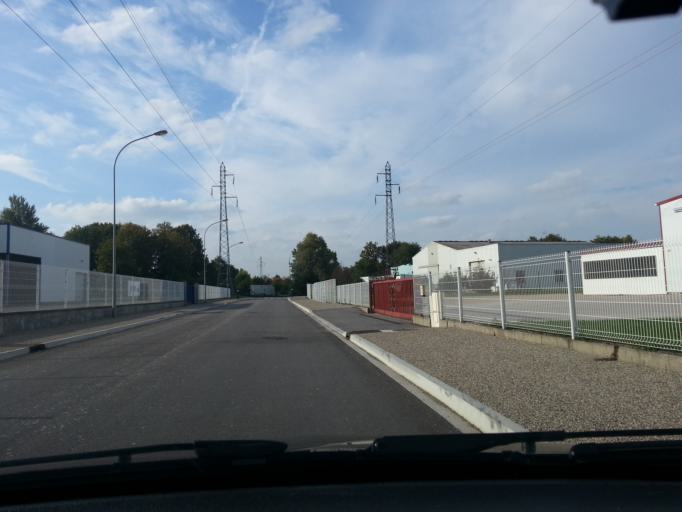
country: FR
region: Bourgogne
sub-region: Departement de Saone-et-Loire
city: Chatenoy-le-Royal
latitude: 46.7972
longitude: 4.7895
